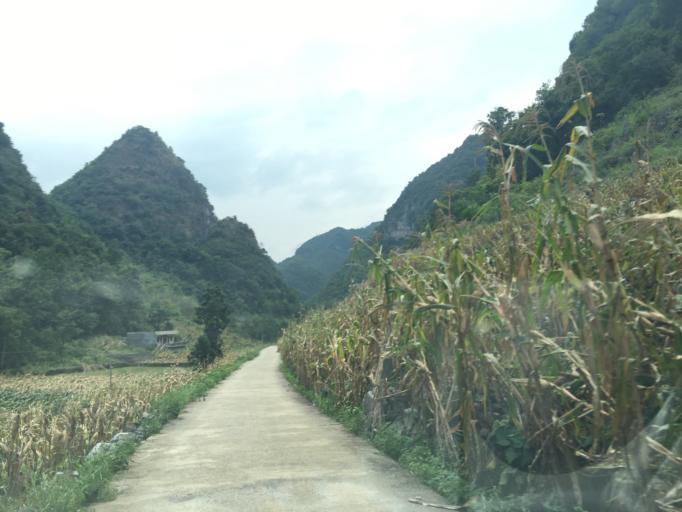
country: CN
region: Guangxi Zhuangzu Zizhiqu
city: Xinzhou
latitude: 25.2310
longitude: 105.6449
